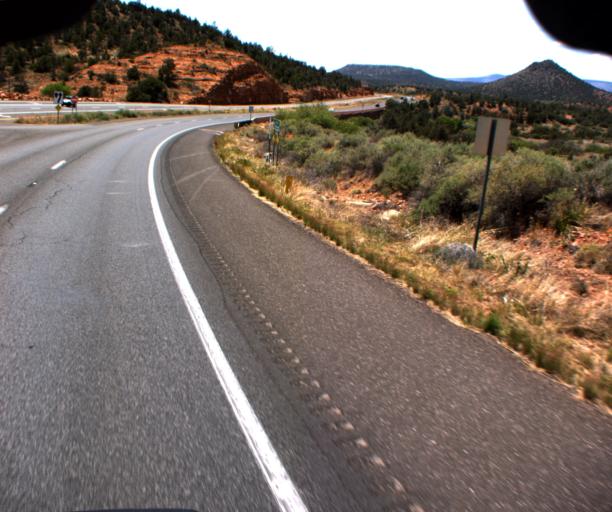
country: US
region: Arizona
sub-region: Yavapai County
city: West Sedona
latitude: 34.8449
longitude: -111.8489
